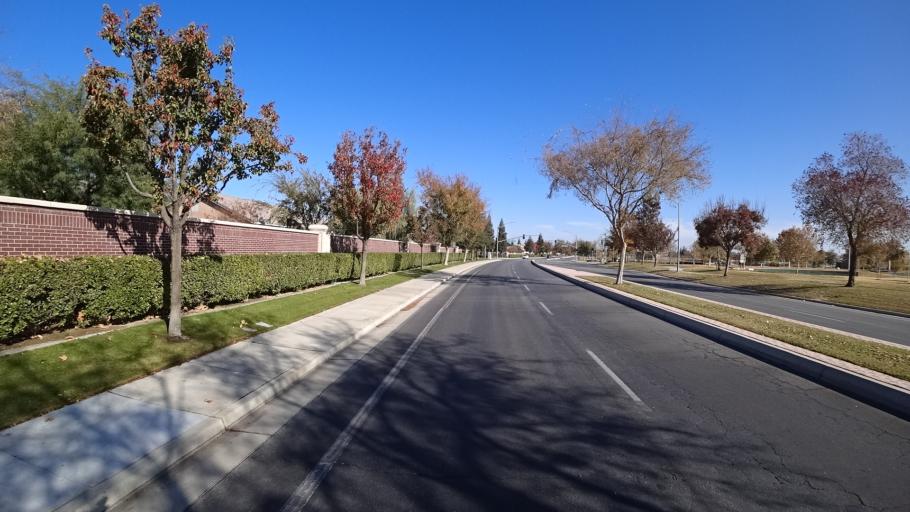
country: US
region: California
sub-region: Kern County
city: Rosedale
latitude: 35.3560
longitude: -119.1355
